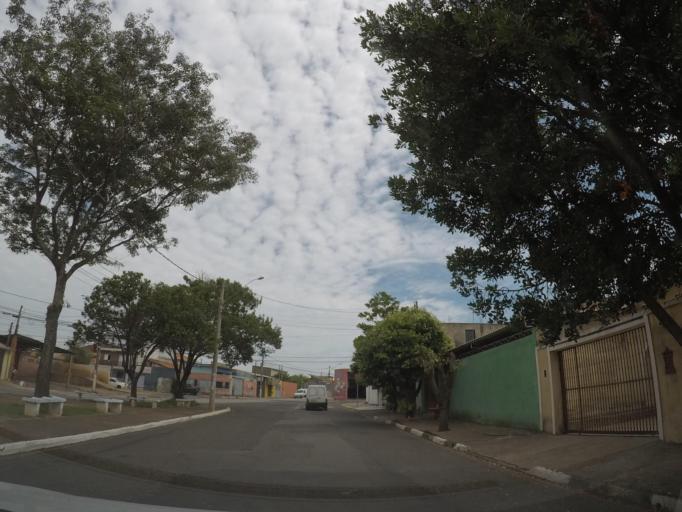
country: BR
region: Sao Paulo
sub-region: Hortolandia
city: Hortolandia
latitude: -22.8352
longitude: -47.1871
